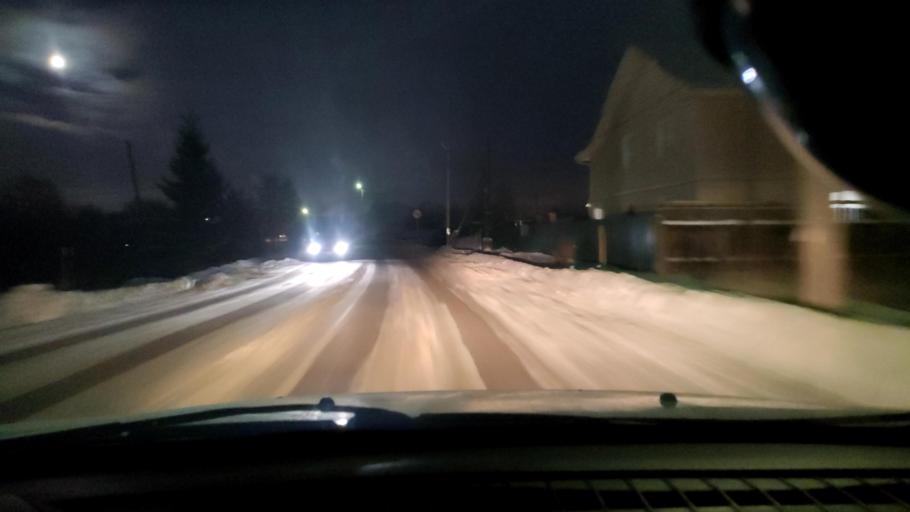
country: RU
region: Perm
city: Kultayevo
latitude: 57.8947
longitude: 55.9433
